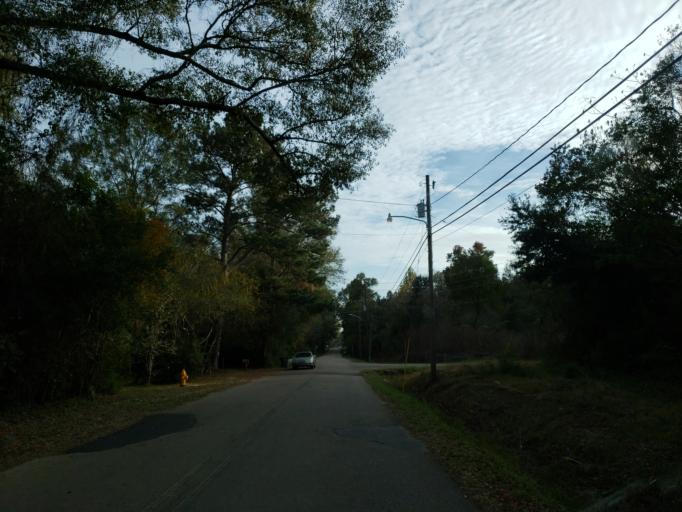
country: US
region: Mississippi
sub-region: Forrest County
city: Hattiesburg
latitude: 31.2968
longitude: -89.2843
